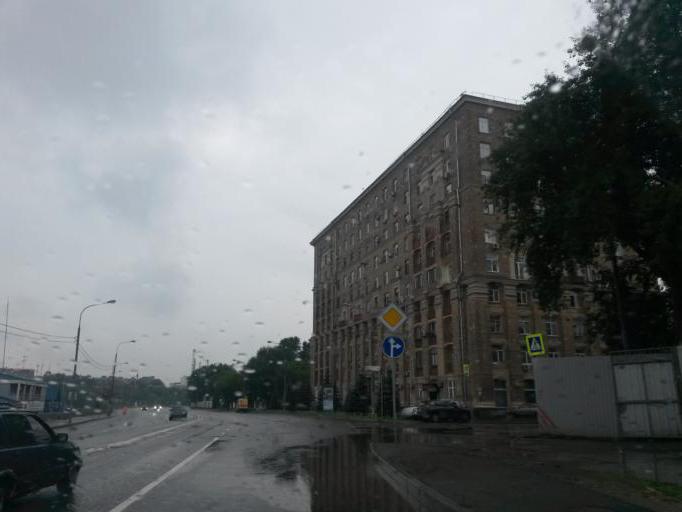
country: RU
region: Moscow
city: Zamoskvorech'ye
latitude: 55.7143
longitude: 37.6470
